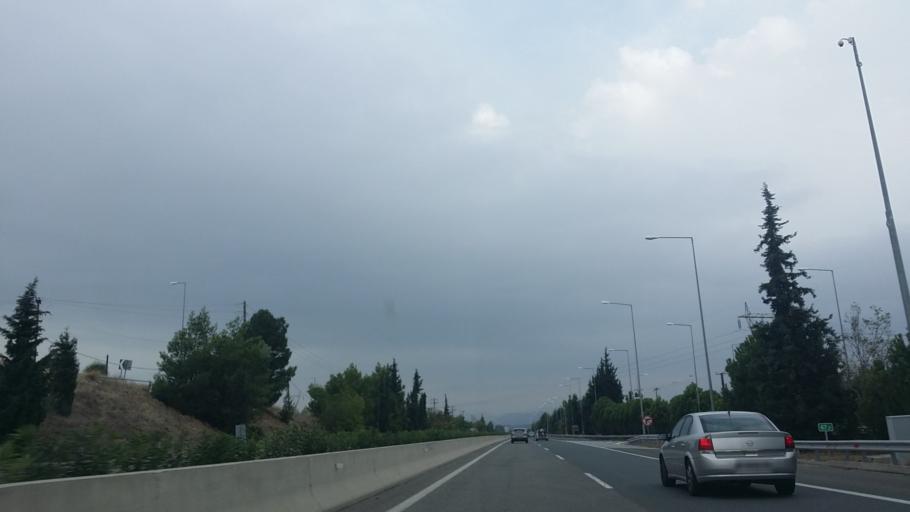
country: GR
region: Central Greece
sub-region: Nomos Voiotias
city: Schimatari
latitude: 38.3553
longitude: 23.5700
